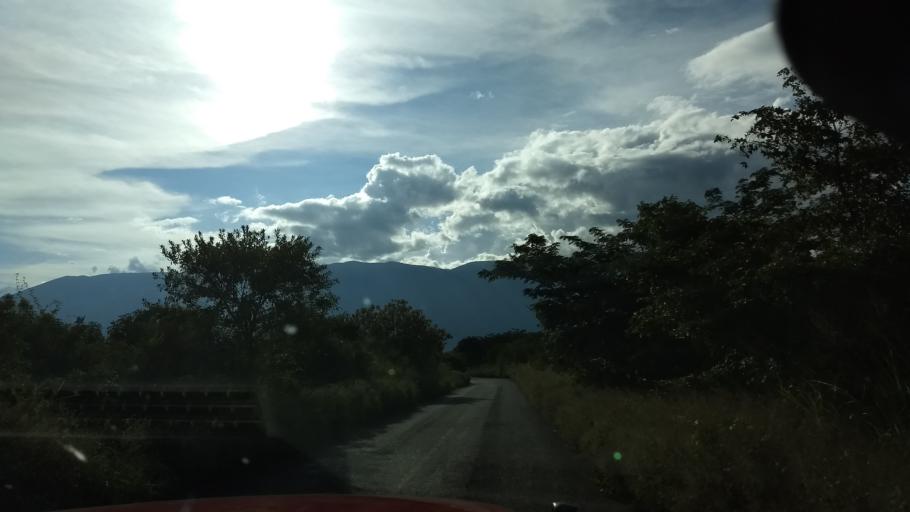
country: MX
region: Colima
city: Suchitlan
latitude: 19.4655
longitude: -103.7818
